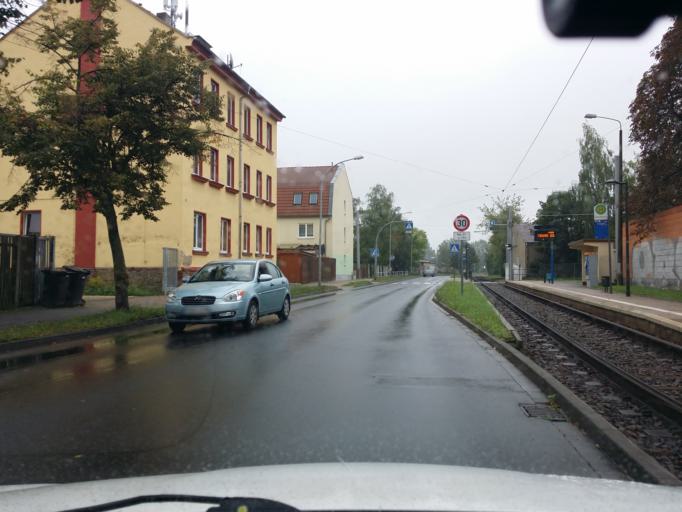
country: DE
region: Saxony
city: Schkeuditz
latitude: 51.3617
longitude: 12.2715
